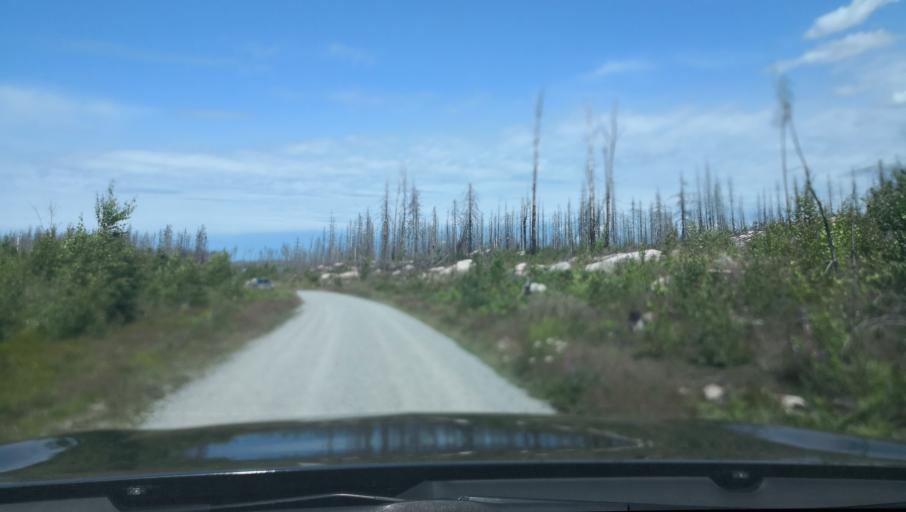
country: SE
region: Vaestmanland
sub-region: Surahammars Kommun
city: Ramnas
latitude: 59.9062
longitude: 16.1465
